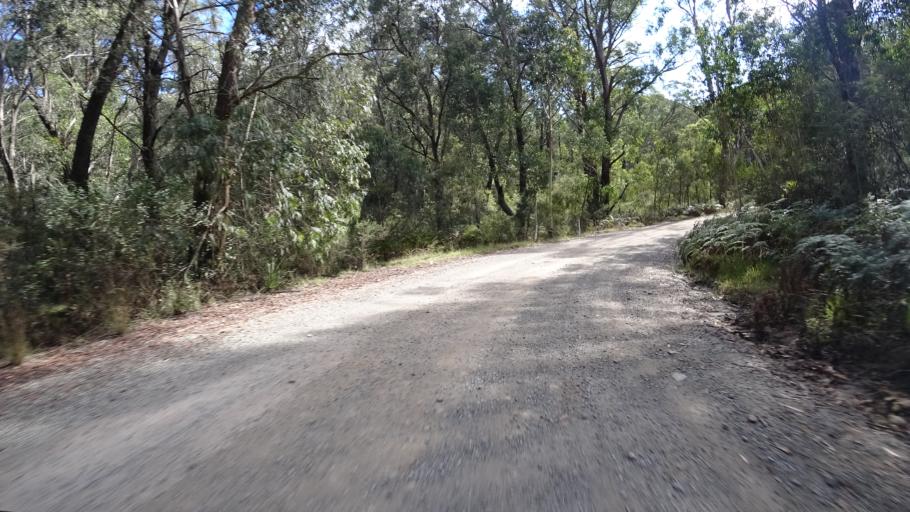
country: AU
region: New South Wales
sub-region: Lithgow
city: Lithgow
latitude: -33.5010
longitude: 150.1675
